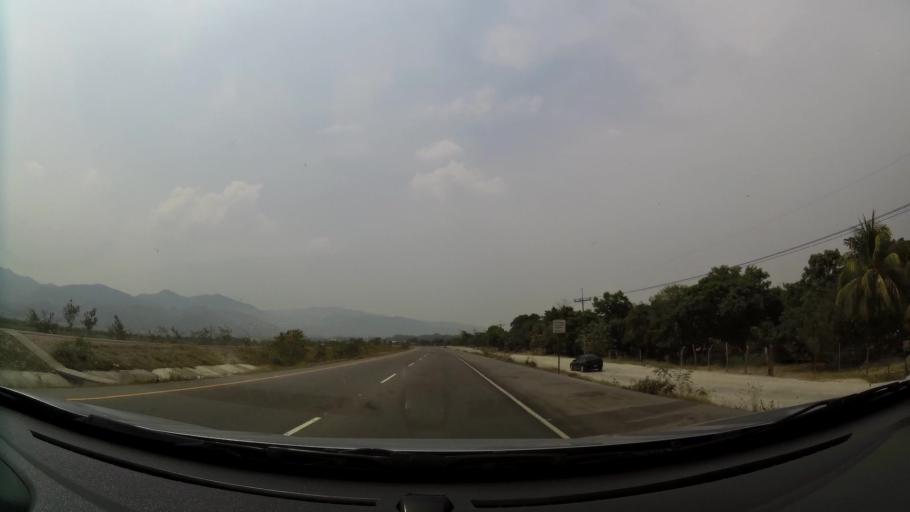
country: HN
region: Cortes
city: El Plan
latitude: 15.2926
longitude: -87.9788
